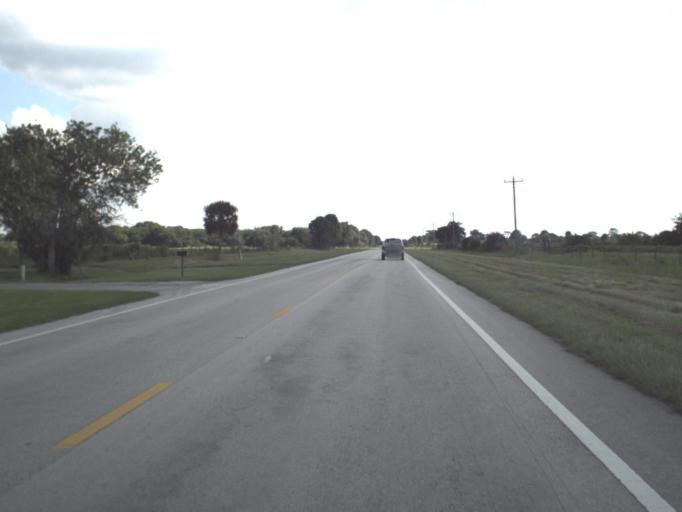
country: US
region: Florida
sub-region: Okeechobee County
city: Okeechobee
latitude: 27.3052
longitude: -80.8999
